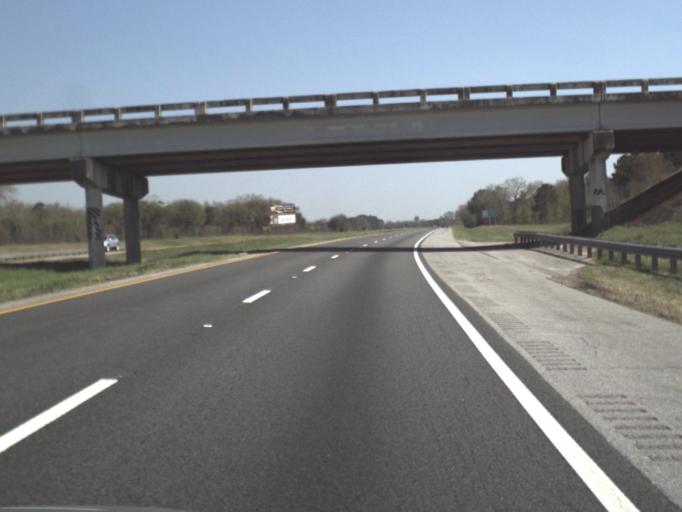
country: US
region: Florida
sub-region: Jackson County
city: Sneads
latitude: 30.6485
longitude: -85.0131
